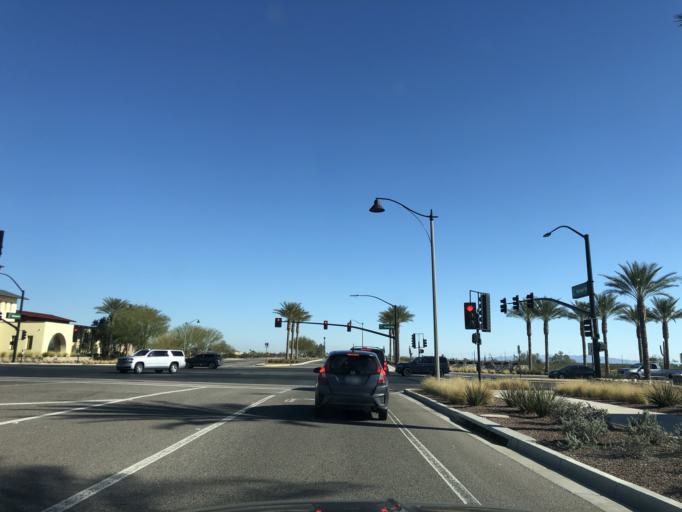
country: US
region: Arizona
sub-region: Maricopa County
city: Citrus Park
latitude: 33.4668
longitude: -112.5050
